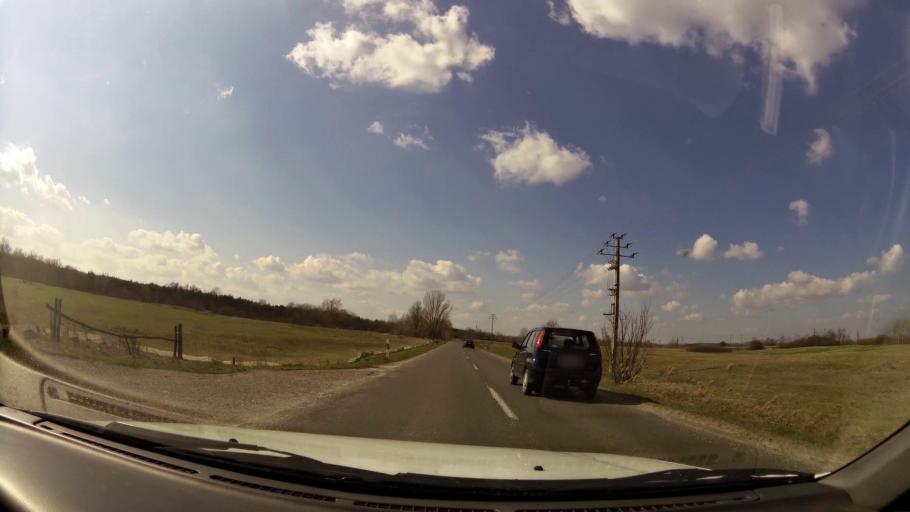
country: HU
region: Pest
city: Farmos
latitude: 47.3563
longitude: 19.8262
